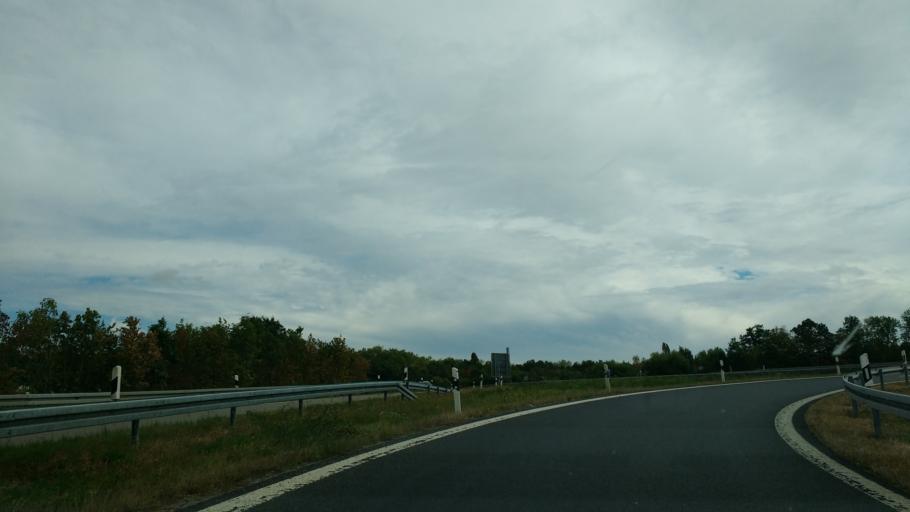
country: DE
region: Bavaria
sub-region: Regierungsbezirk Unterfranken
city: Sennfeld
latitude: 50.0256
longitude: 10.2390
